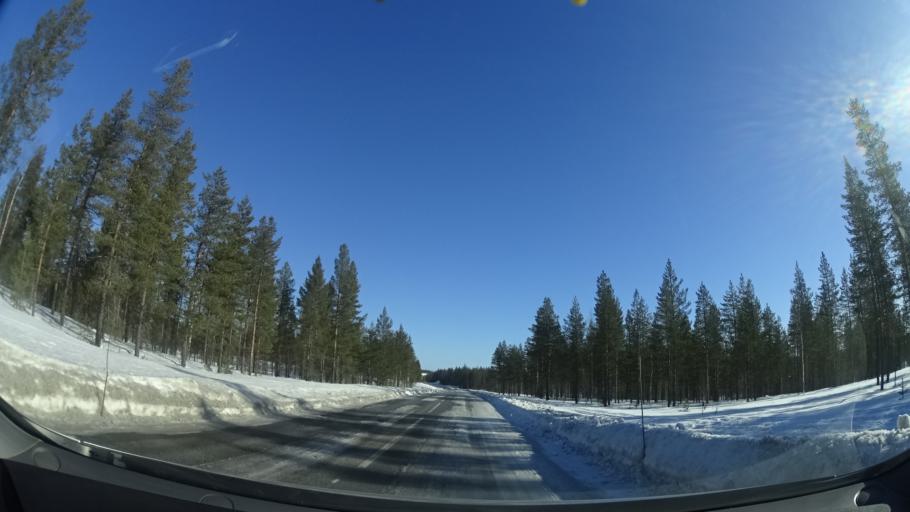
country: SE
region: Vaesterbotten
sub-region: Skelleftea Kommun
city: Langsele
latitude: 65.1263
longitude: 20.1229
